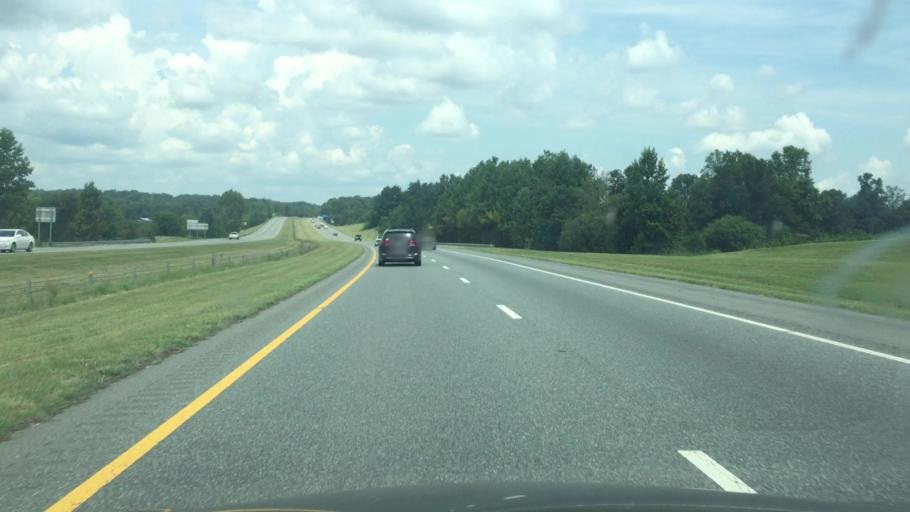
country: US
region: North Carolina
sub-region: Montgomery County
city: Biscoe
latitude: 35.4915
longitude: -79.7799
